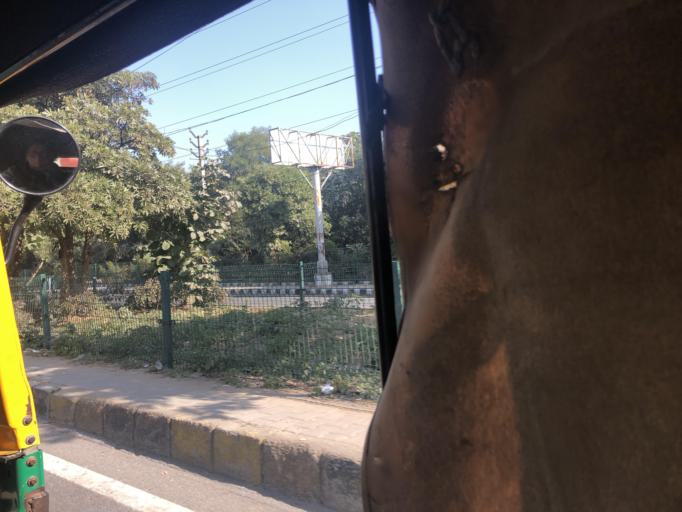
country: IN
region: Haryana
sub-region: Gurgaon
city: Gurgaon
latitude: 28.4303
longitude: 77.0913
